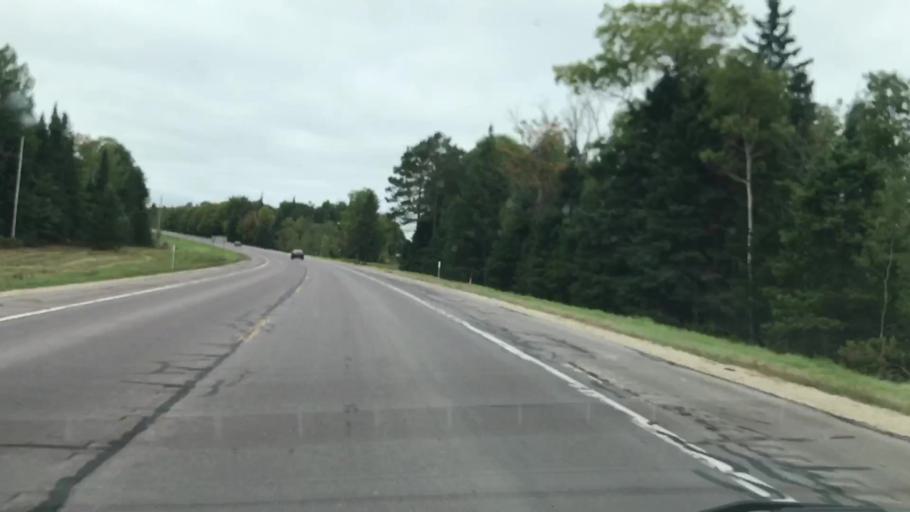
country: US
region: Michigan
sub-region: Schoolcraft County
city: Manistique
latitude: 46.1007
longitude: -85.9365
